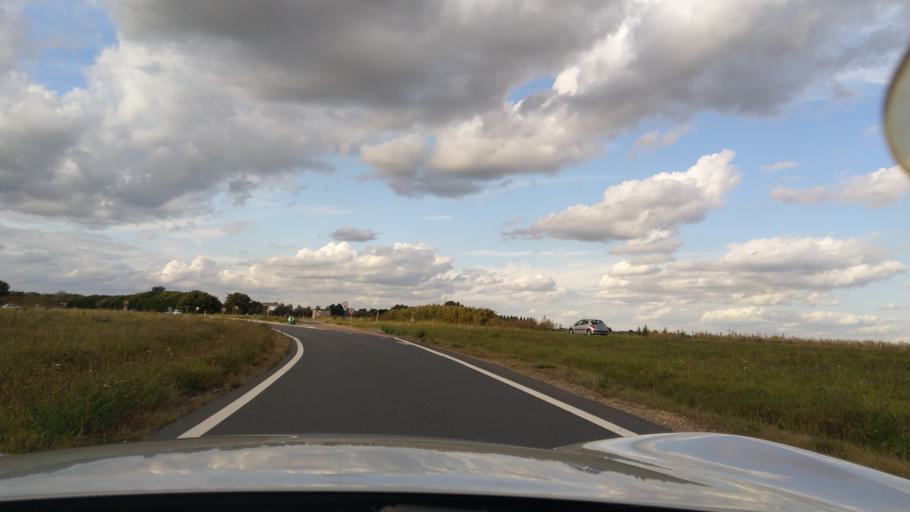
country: FR
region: Ile-de-France
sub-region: Departement de Seine-et-Marne
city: Moussy-le-Neuf
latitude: 49.0250
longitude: 2.5842
